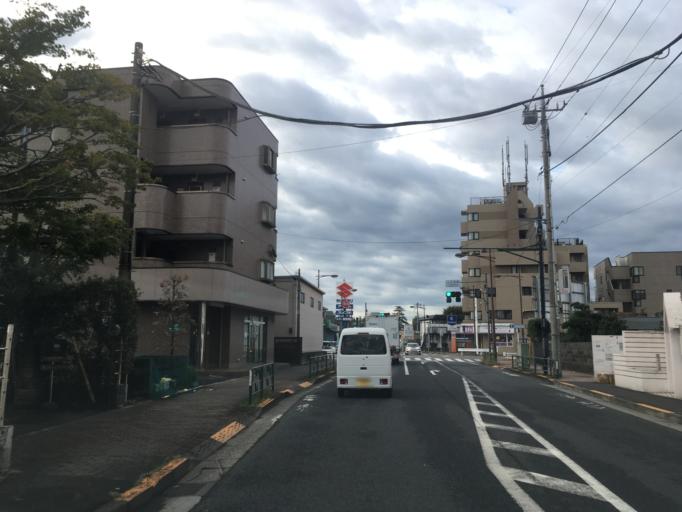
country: JP
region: Tokyo
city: Kokubunji
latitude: 35.7179
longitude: 139.4651
